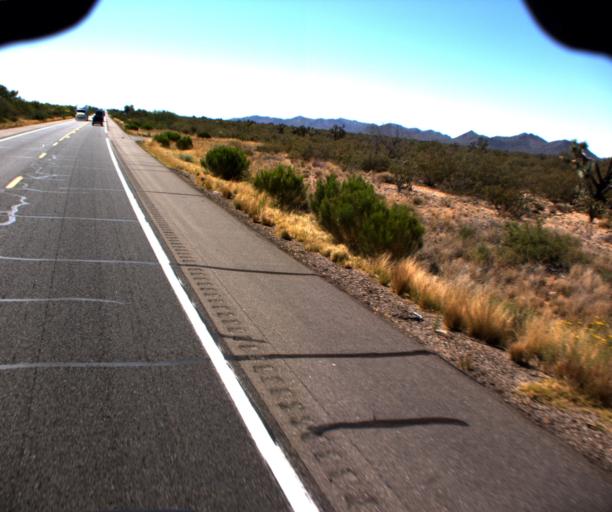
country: US
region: Arizona
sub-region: Yavapai County
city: Congress
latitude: 34.1730
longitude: -113.0220
